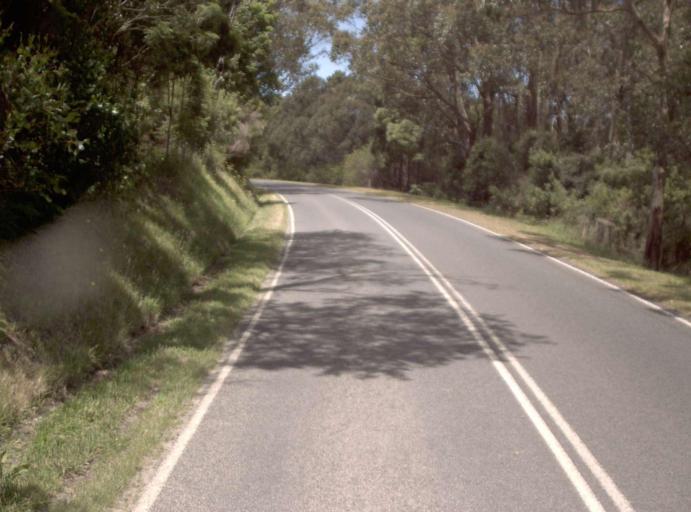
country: AU
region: Victoria
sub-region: Bass Coast
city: North Wonthaggi
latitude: -38.7298
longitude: 146.1218
